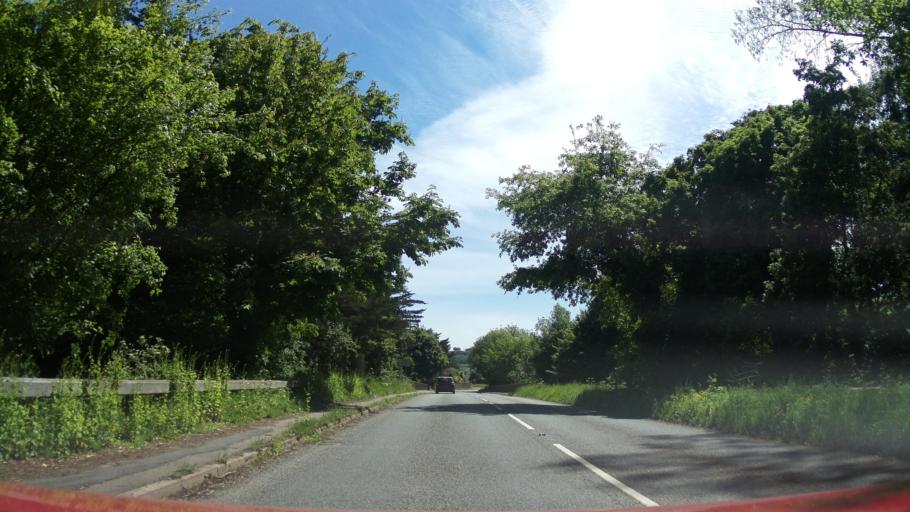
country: GB
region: England
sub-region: Devon
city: Honiton
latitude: 50.8027
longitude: -3.2003
